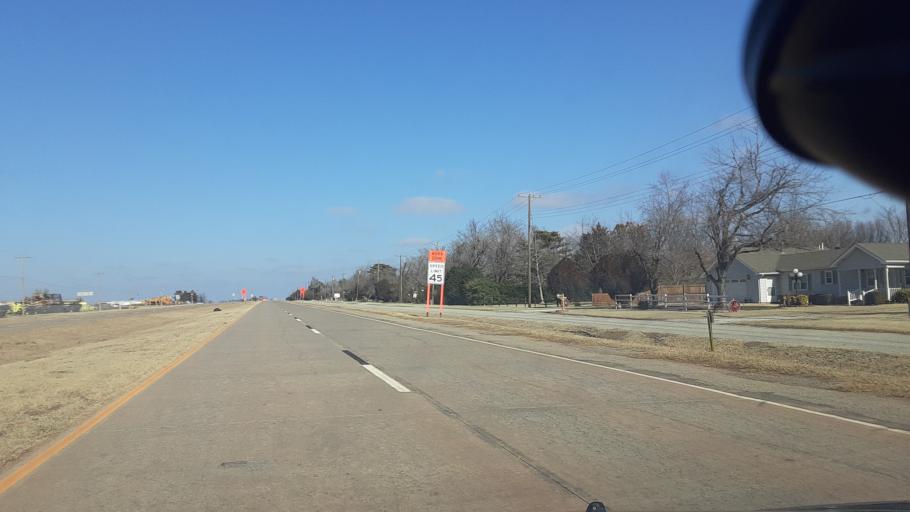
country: US
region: Oklahoma
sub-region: Garfield County
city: Enid
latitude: 36.4504
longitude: -97.8729
